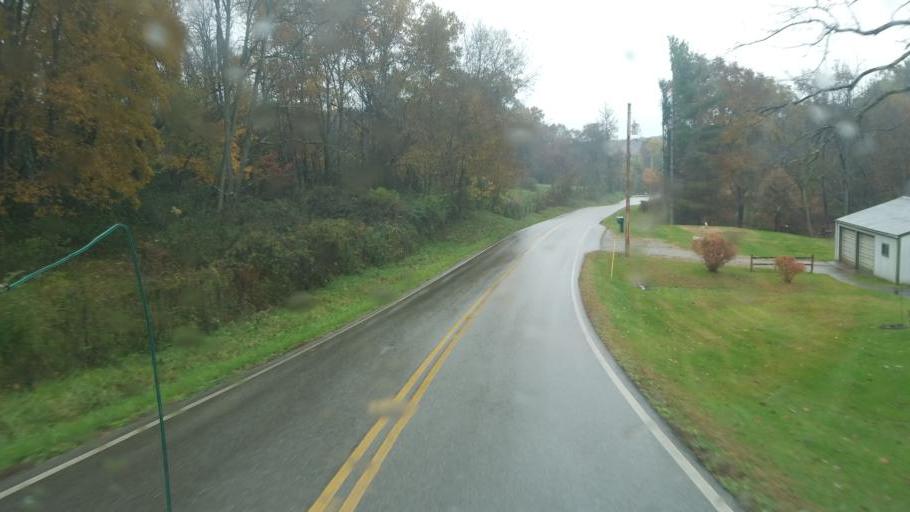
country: US
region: West Virginia
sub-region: Wood County
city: Blennerhassett
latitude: 39.3245
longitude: -81.6221
